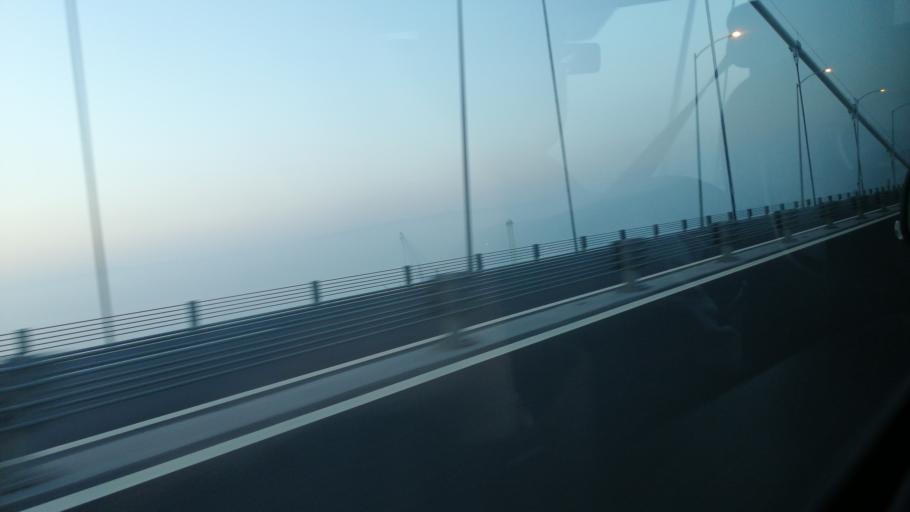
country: TR
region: Kocaeli
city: Tavsanli
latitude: 40.7650
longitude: 29.5175
